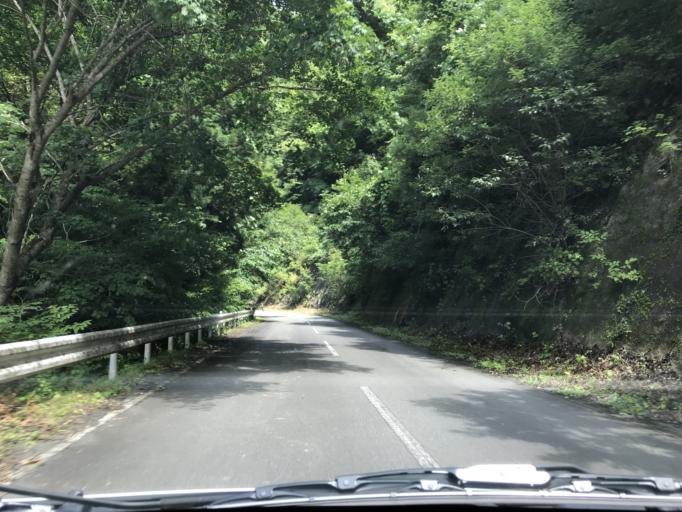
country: JP
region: Iwate
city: Tono
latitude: 39.0747
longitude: 141.4082
